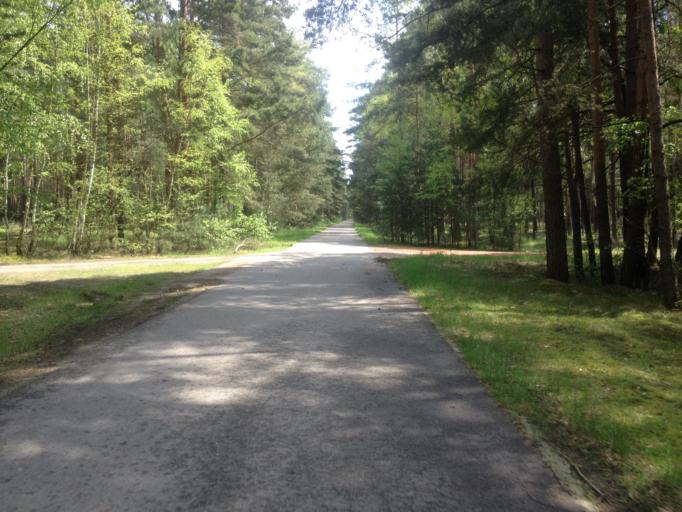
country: DE
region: Brandenburg
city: Briesen
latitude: 51.8087
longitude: 14.2553
